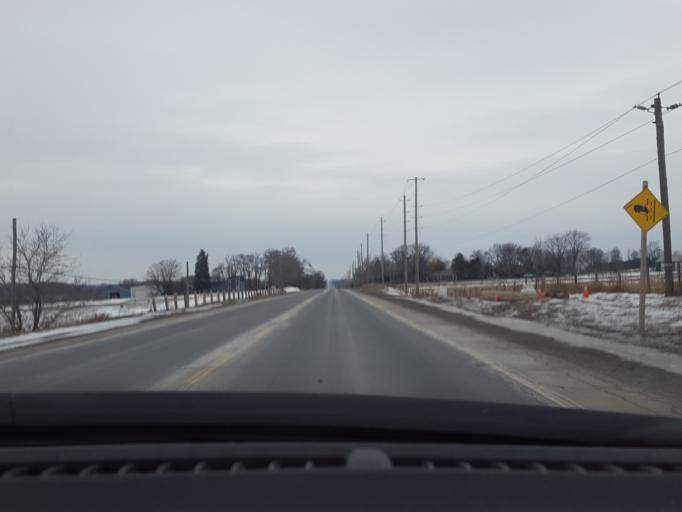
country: CA
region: Ontario
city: Keswick
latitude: 44.1721
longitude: -79.4330
